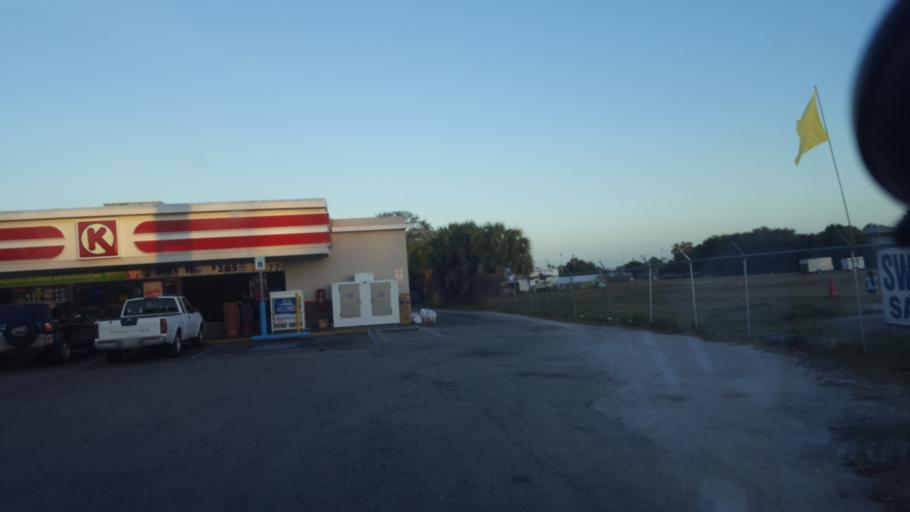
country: US
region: Florida
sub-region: Sarasota County
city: Sarasota
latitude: 27.3357
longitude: -82.5139
